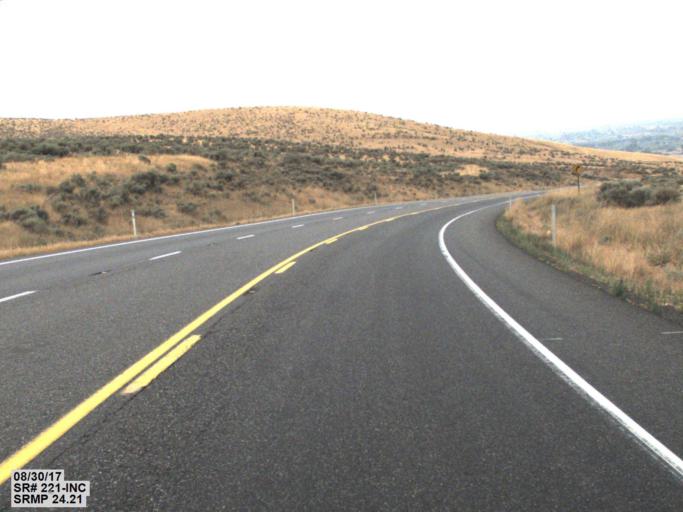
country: US
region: Washington
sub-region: Benton County
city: Prosser
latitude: 46.1994
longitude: -119.7177
